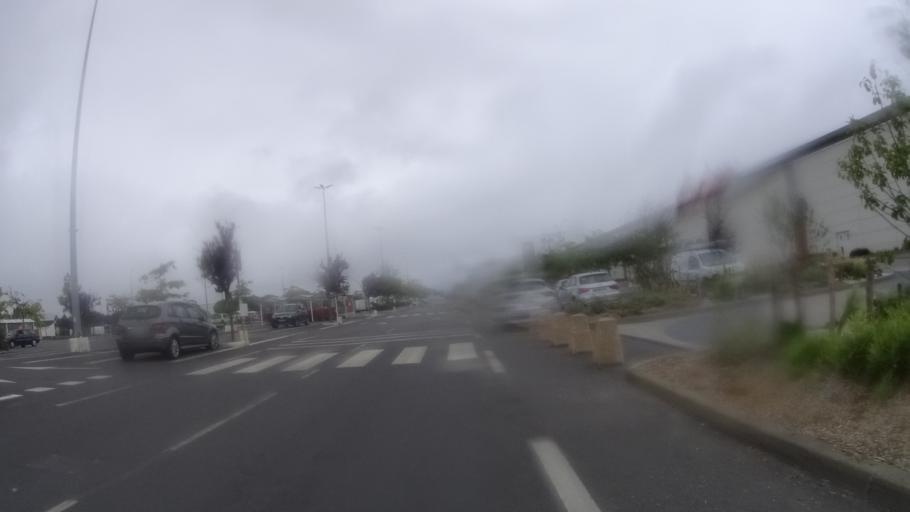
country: FR
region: Pays de la Loire
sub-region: Departement de la Loire-Atlantique
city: Saint-Nazaire
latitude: 47.3017
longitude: -2.2087
